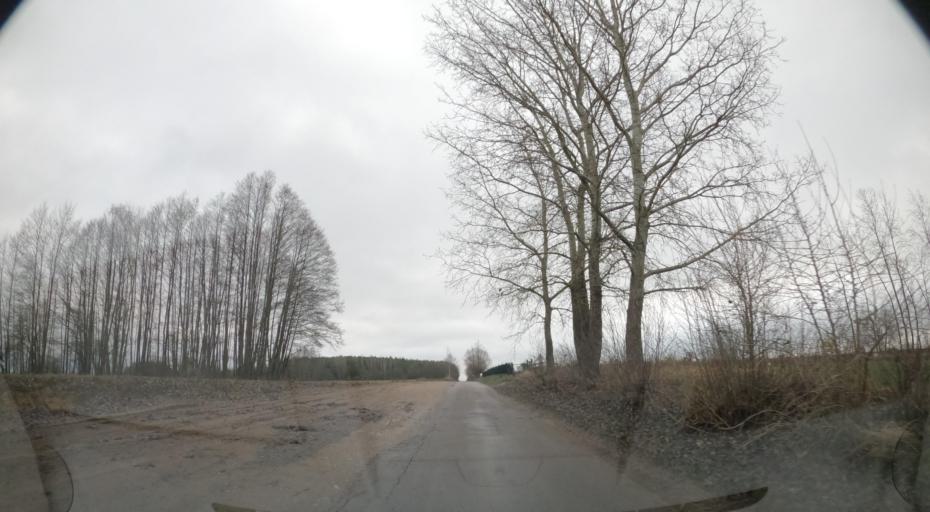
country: PL
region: Greater Poland Voivodeship
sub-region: Powiat pilski
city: Wysoka
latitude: 53.2551
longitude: 17.1301
